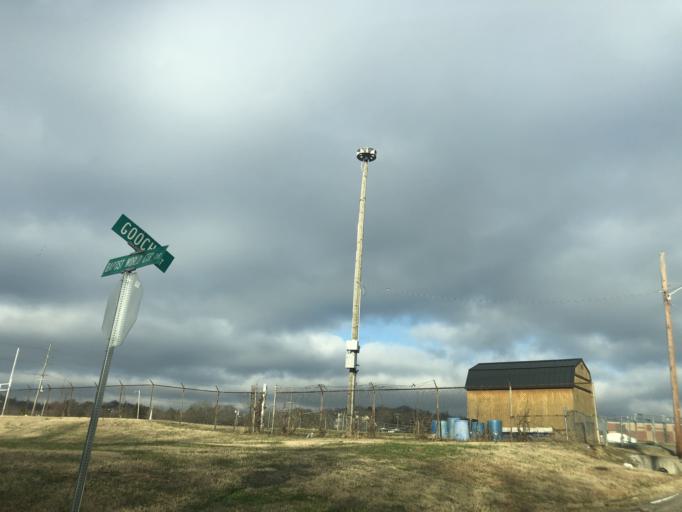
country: US
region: Tennessee
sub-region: Davidson County
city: Nashville
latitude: 36.2060
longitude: -86.7906
